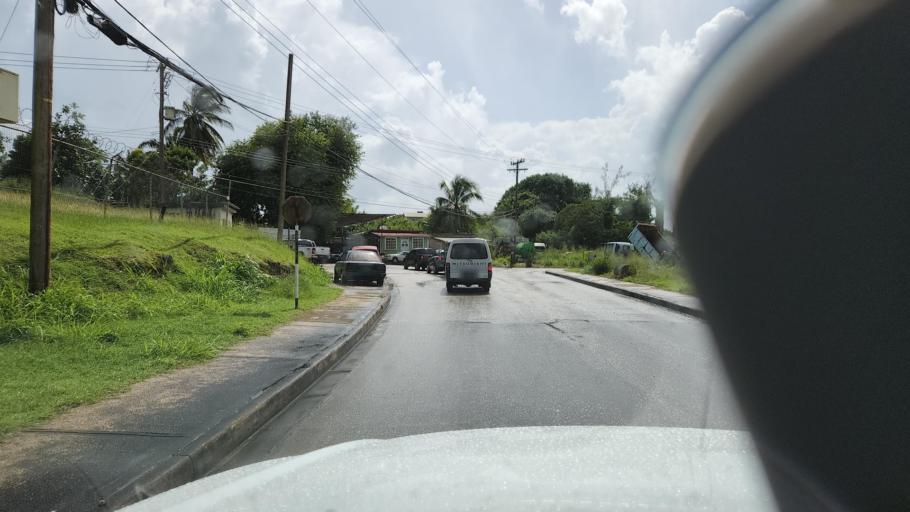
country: BB
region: Saint Michael
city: Bridgetown
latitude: 13.1068
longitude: -59.5695
